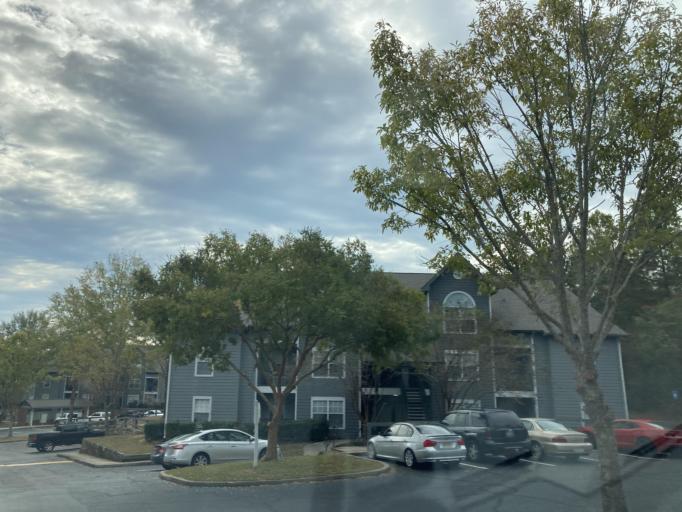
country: US
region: Mississippi
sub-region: Lamar County
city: West Hattiesburg
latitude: 31.3023
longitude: -89.3762
